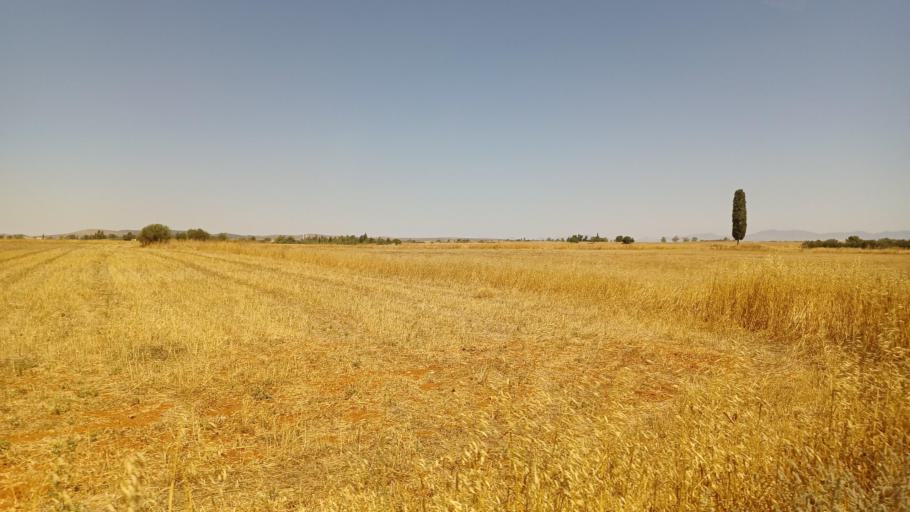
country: CY
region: Larnaka
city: Xylotymbou
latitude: 35.0313
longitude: 33.7309
